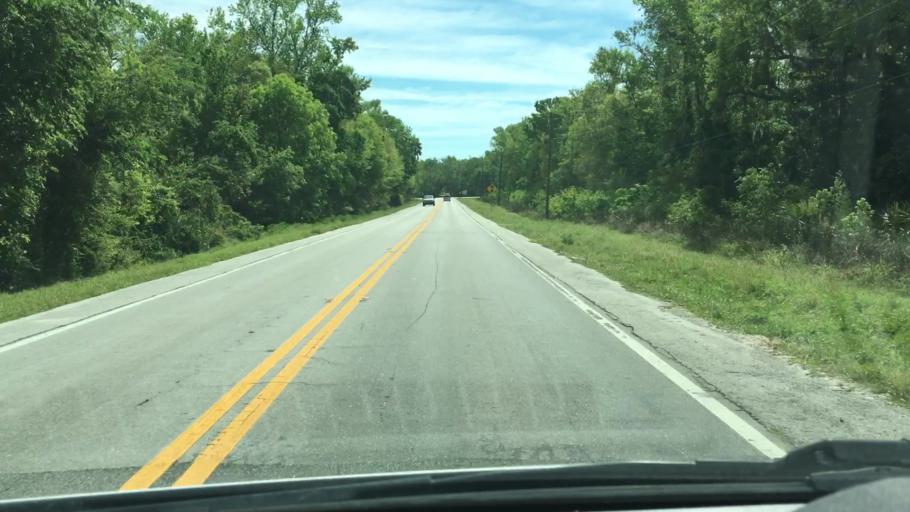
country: US
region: Florida
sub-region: Lake County
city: Lake Mack-Forest Hills
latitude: 29.0076
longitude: -81.3891
